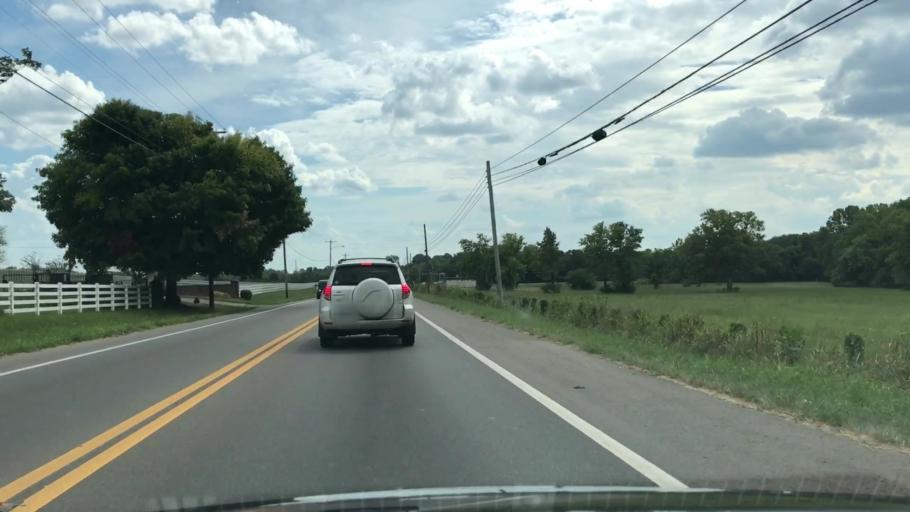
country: US
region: Tennessee
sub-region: Maury County
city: Spring Hill
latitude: 35.7634
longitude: -86.9204
